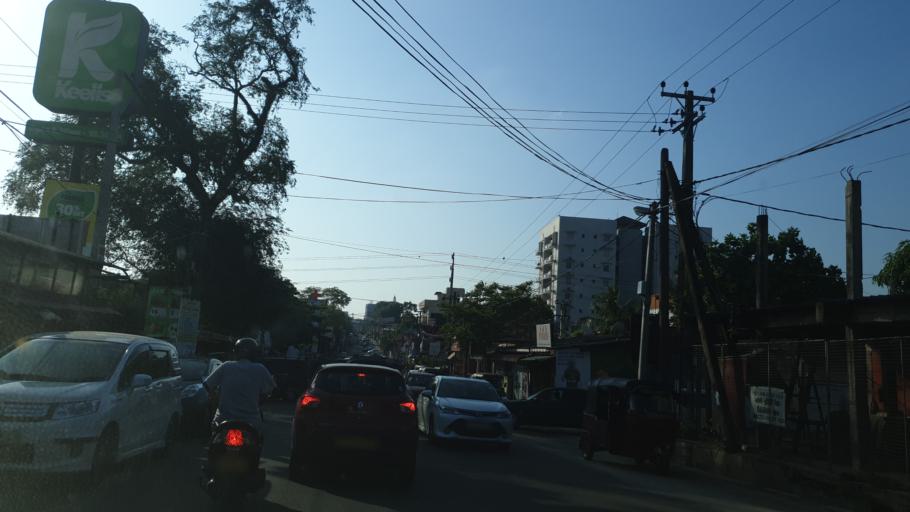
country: LK
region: Western
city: Galkissa
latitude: 6.8496
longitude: 79.8778
